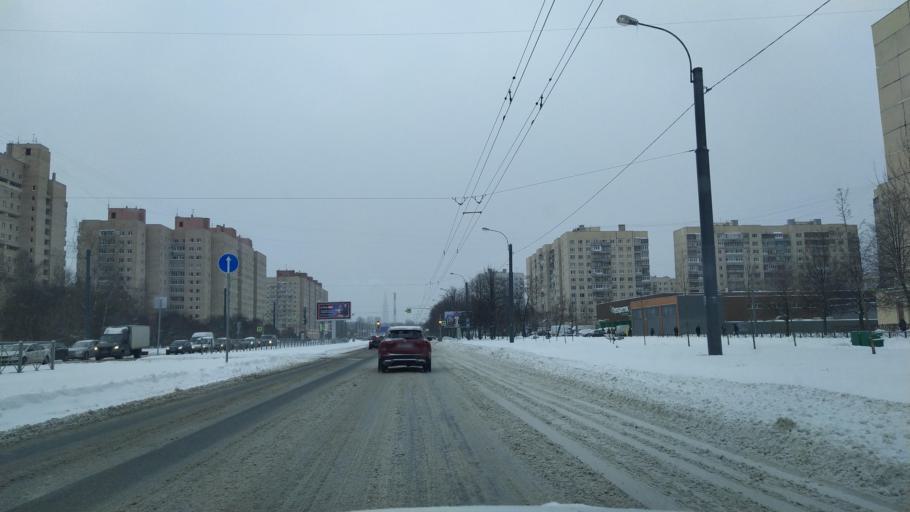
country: RU
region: St.-Petersburg
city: Novaya Derevnya
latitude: 59.9999
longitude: 30.2890
